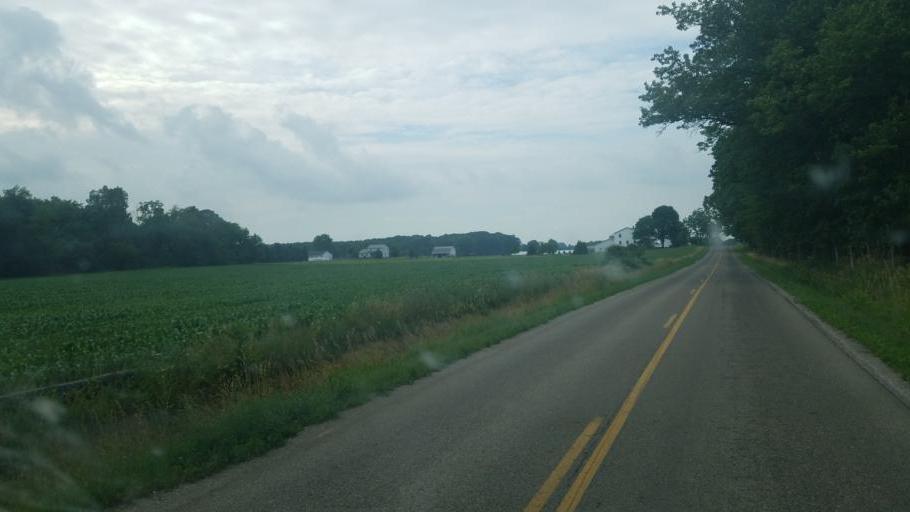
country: US
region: Ohio
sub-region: Wayne County
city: Apple Creek
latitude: 40.7752
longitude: -81.8242
